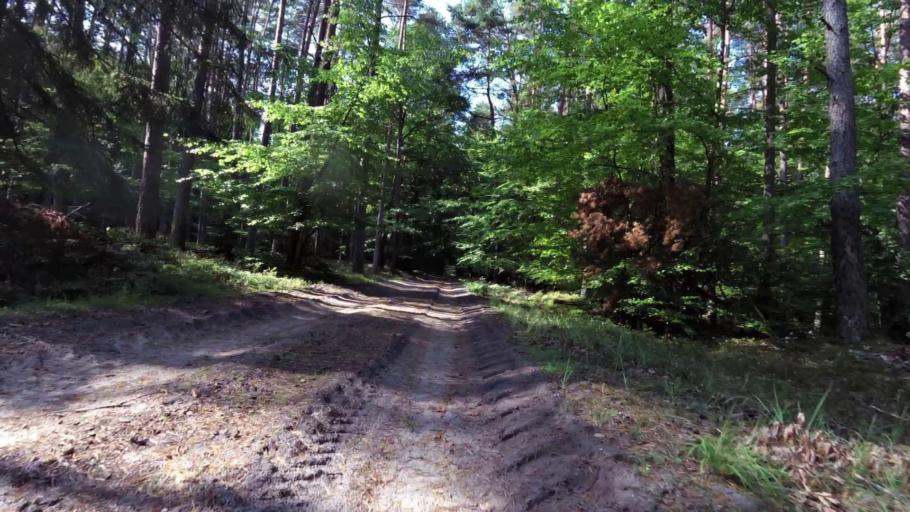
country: PL
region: West Pomeranian Voivodeship
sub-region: Powiat kamienski
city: Miedzyzdroje
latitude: 53.9192
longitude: 14.5057
